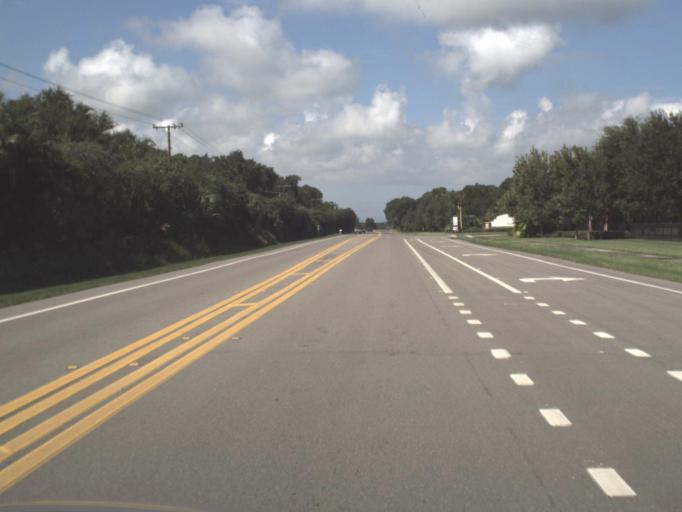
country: US
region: Florida
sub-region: Sarasota County
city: Lake Sarasota
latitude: 27.2457
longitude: -82.3655
